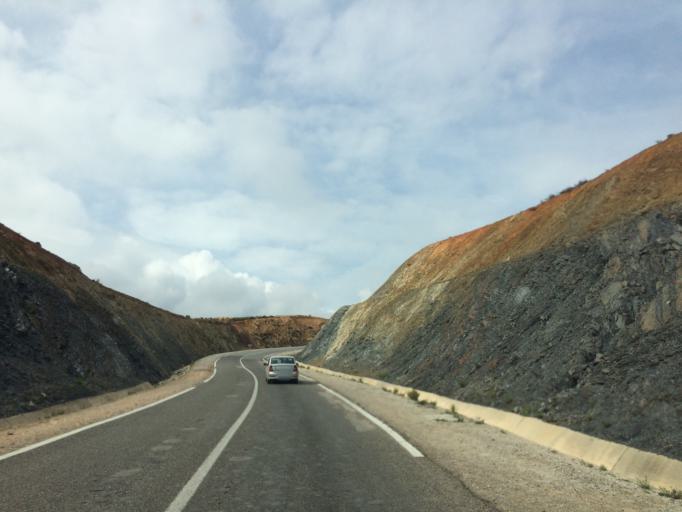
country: ES
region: Ceuta
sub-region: Ceuta
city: Ceuta
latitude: 35.8667
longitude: -5.3488
